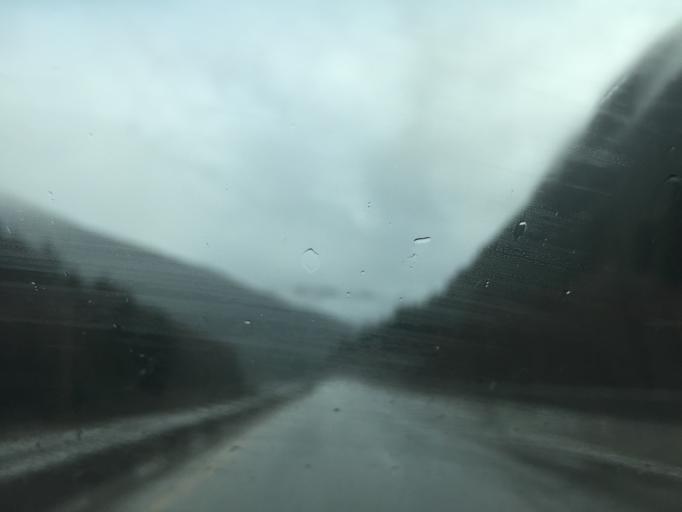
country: CA
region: British Columbia
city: Hope
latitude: 49.5161
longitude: -121.2038
